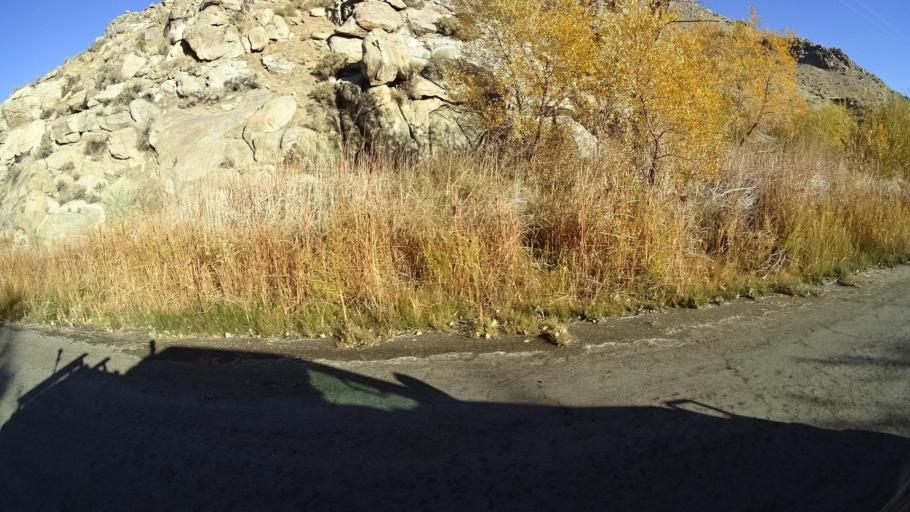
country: US
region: California
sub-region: Kern County
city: Weldon
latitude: 35.5753
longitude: -118.2515
